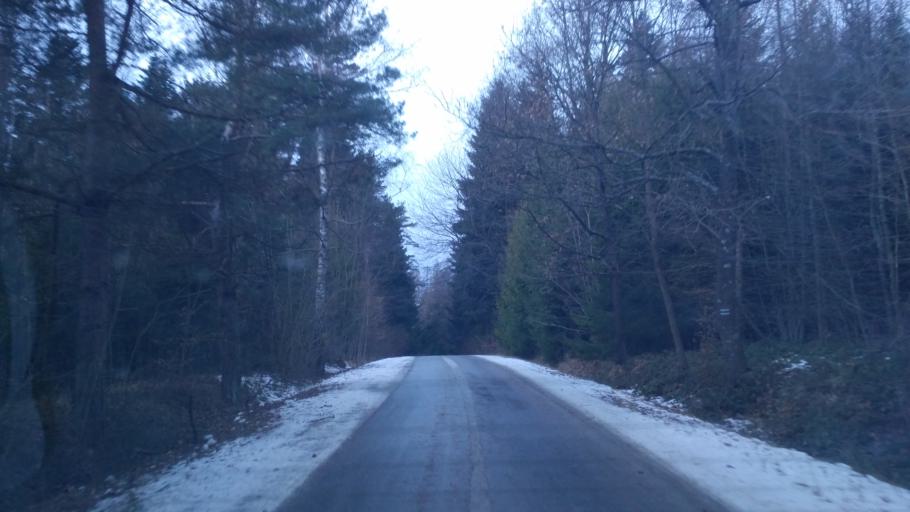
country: PL
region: Subcarpathian Voivodeship
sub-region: Powiat rzeszowski
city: Hyzne
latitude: 49.8964
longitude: 22.1612
